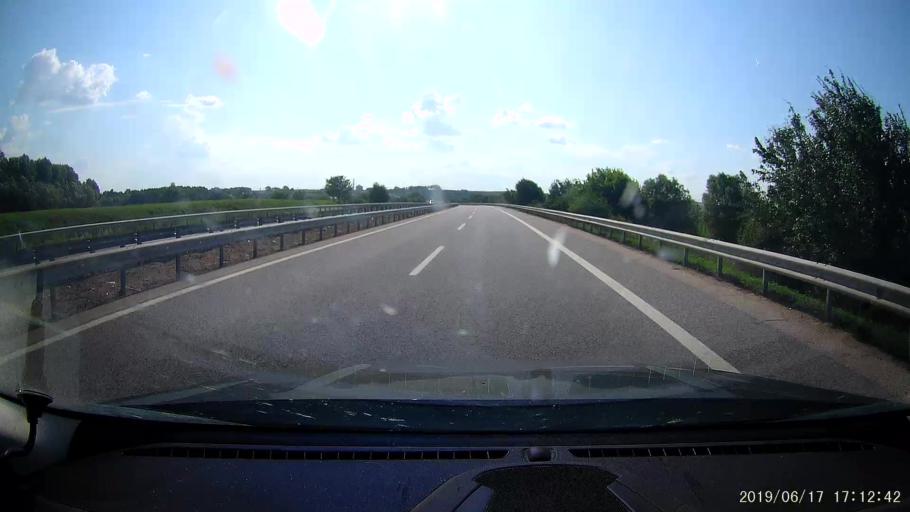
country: TR
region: Edirne
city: Edirne
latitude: 41.7009
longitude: 26.5569
